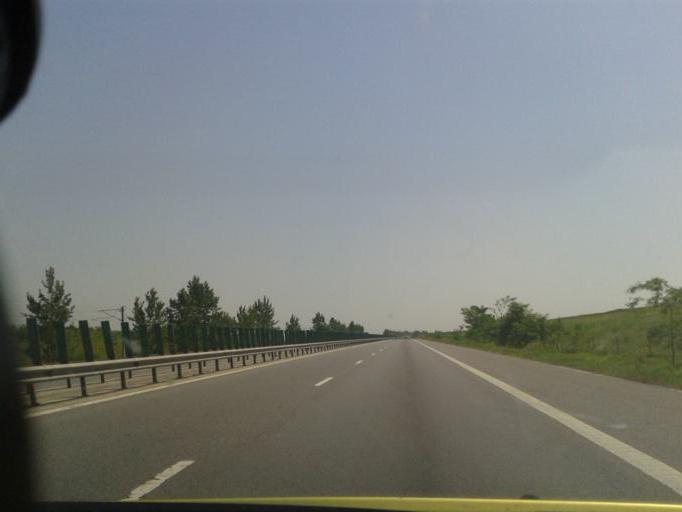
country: RO
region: Calarasi
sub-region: Comuna Sarulesti
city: Sarulesti-Gara
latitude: 44.4455
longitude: 26.6980
